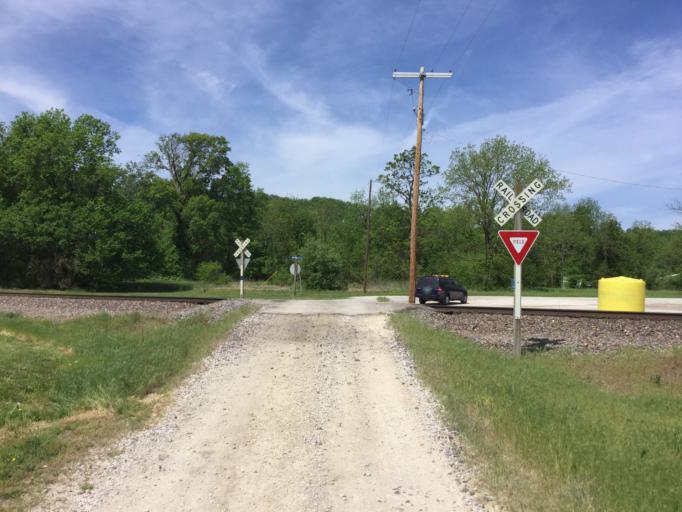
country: US
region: Kansas
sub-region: Coffey County
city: Burlington
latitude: 38.0759
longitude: -95.6316
